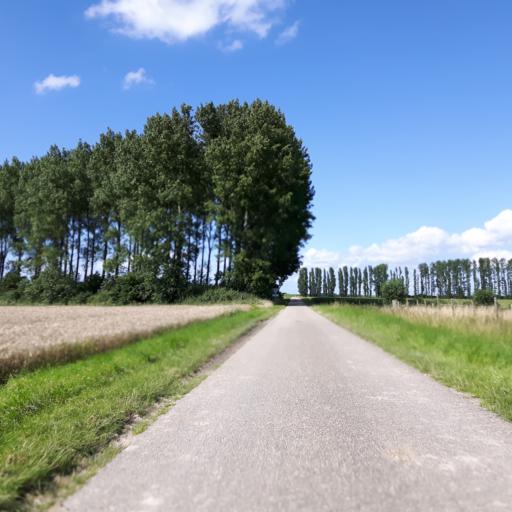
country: NL
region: Zeeland
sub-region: Gemeente Goes
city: Goes
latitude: 51.5313
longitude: 3.8836
